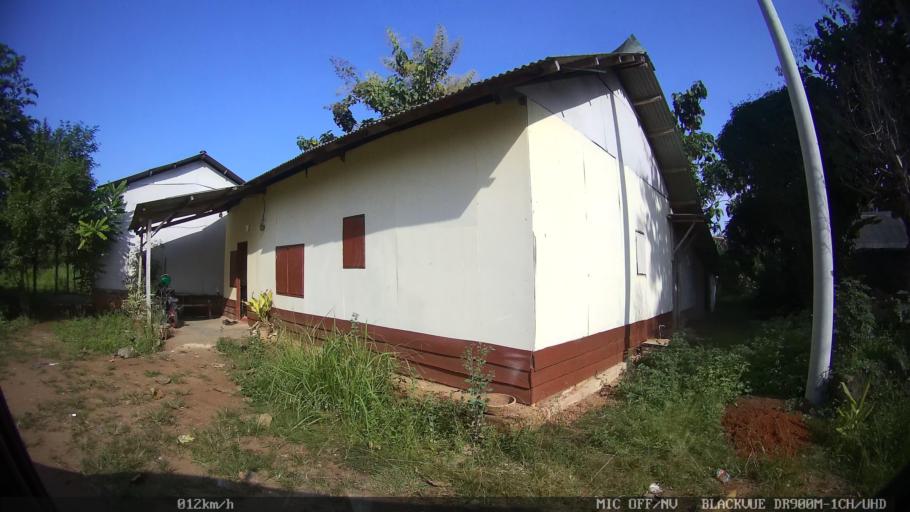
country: ID
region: Lampung
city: Kedaton
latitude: -5.3756
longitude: 105.2320
